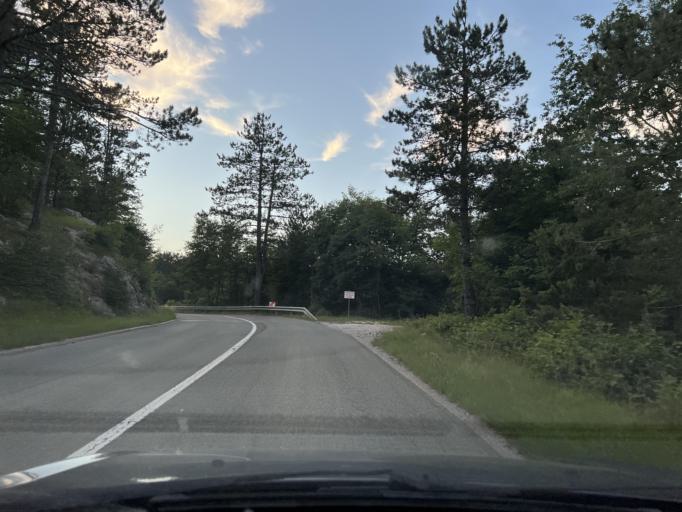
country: HR
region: Primorsko-Goranska
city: Klana
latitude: 45.4411
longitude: 14.3518
